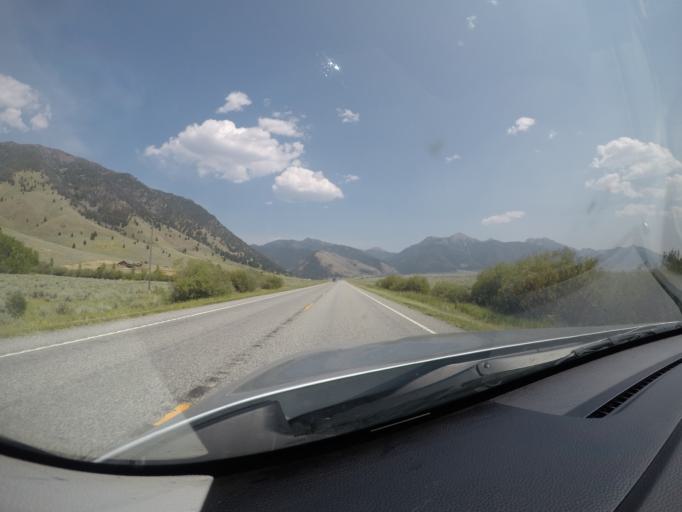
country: US
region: Montana
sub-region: Gallatin County
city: West Yellowstone
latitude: 44.8300
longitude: -111.4768
